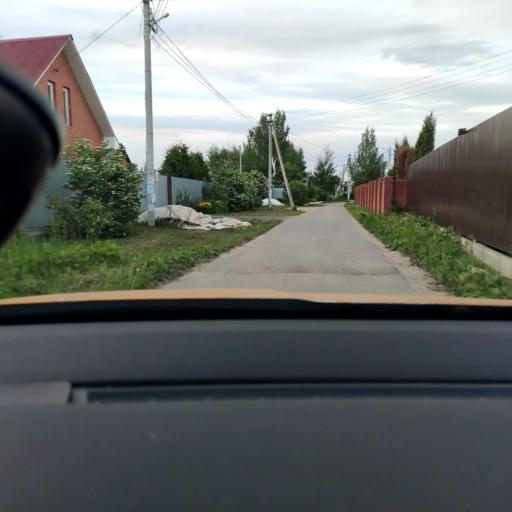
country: RU
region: Moskovskaya
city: Andreyevskoye
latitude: 55.5186
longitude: 37.9644
